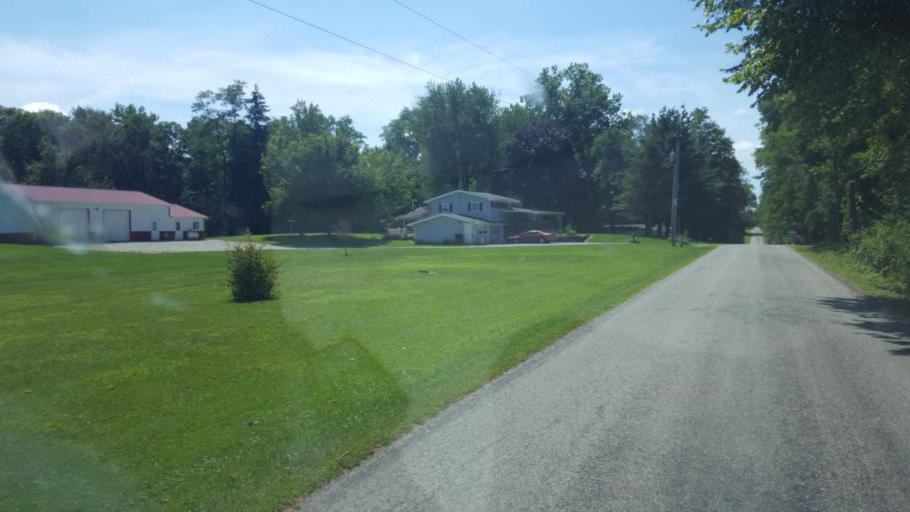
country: US
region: Ohio
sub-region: Knox County
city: Centerburg
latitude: 40.4191
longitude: -82.7678
